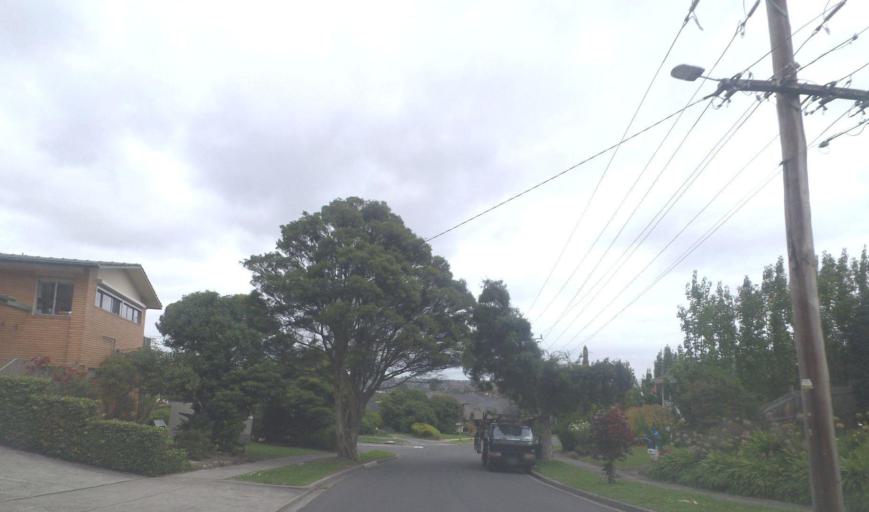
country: AU
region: Victoria
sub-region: Manningham
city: Templestowe Lower
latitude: -37.7779
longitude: 145.1176
